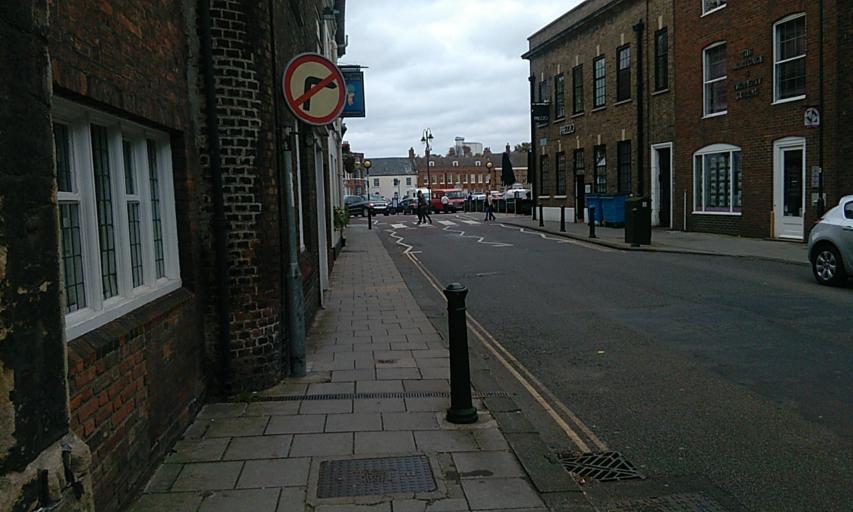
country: GB
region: England
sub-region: Norfolk
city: King's Lynn
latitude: 52.7555
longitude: 0.3937
